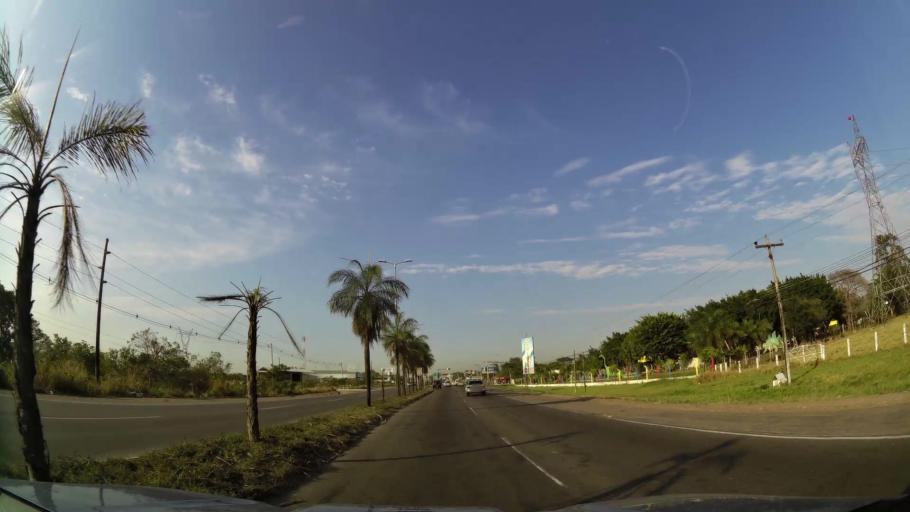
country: BO
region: Santa Cruz
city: Santa Cruz de la Sierra
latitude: -17.6736
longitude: -63.1588
